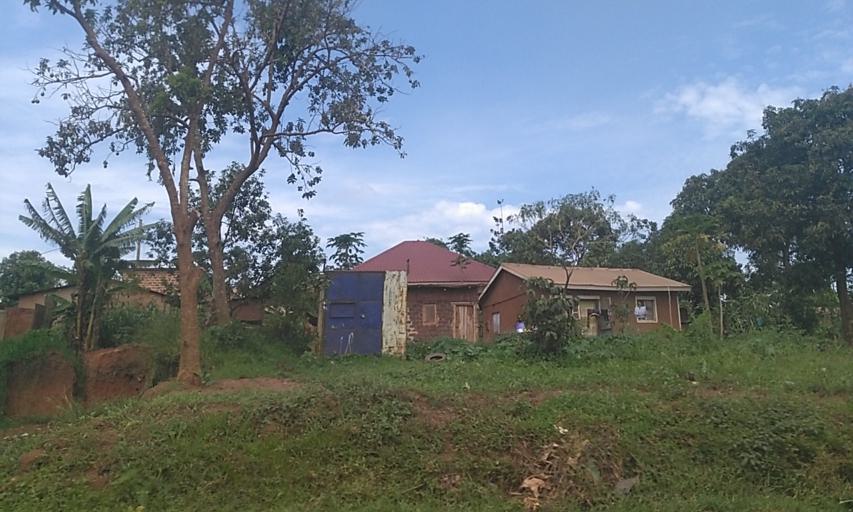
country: UG
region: Central Region
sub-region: Wakiso District
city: Kajansi
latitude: 0.2792
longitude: 32.5164
